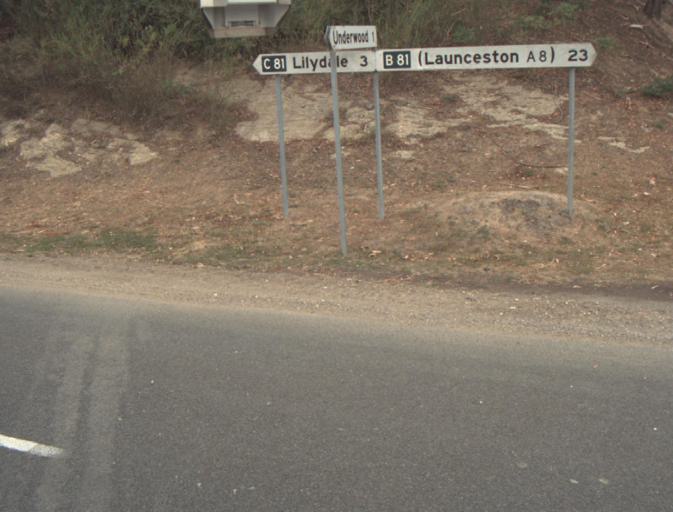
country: AU
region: Tasmania
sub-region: Launceston
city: Mayfield
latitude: -41.2864
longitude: 147.2180
